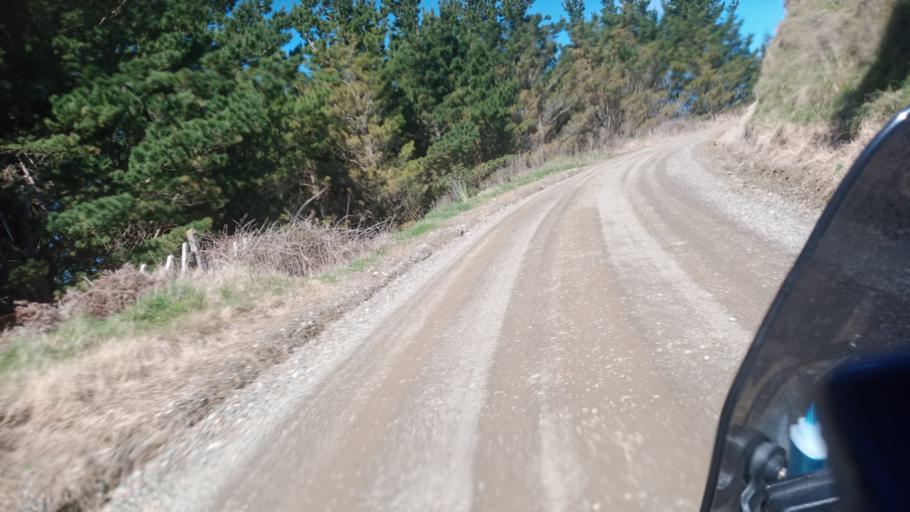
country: NZ
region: Gisborne
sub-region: Gisborne District
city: Gisborne
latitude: -39.1726
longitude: 177.9043
